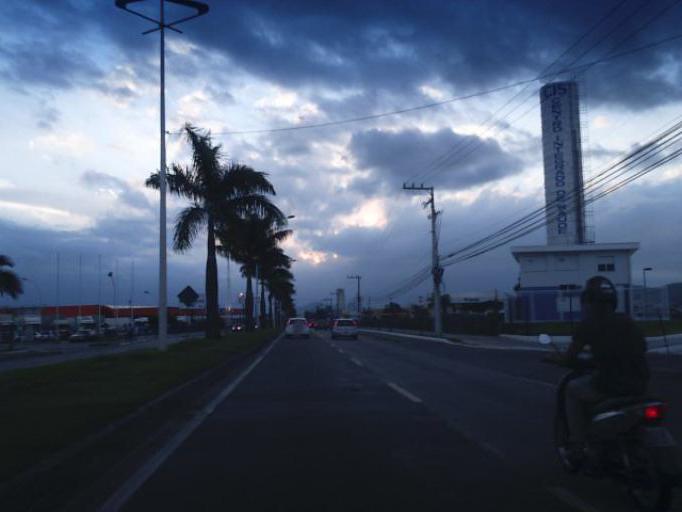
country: BR
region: Santa Catarina
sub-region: Itajai
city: Itajai
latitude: -26.9112
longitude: -48.6866
